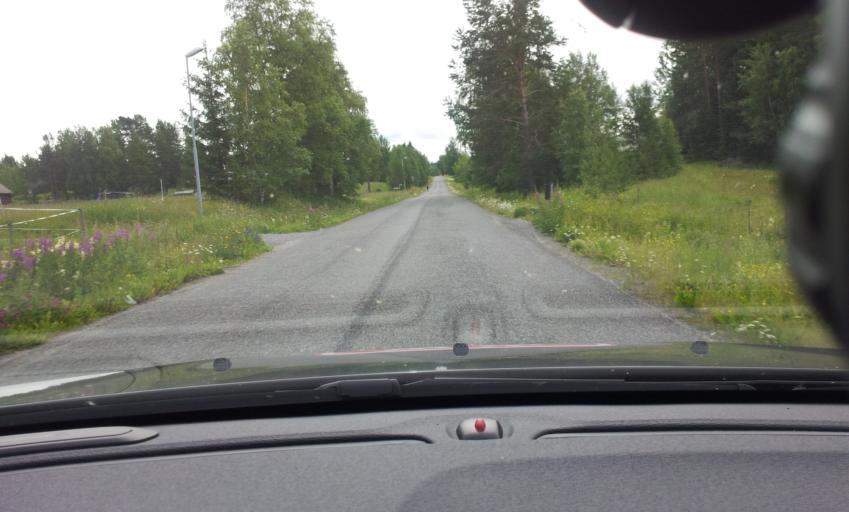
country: SE
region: Jaemtland
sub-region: OEstersunds Kommun
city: Brunflo
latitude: 62.9794
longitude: 14.8933
